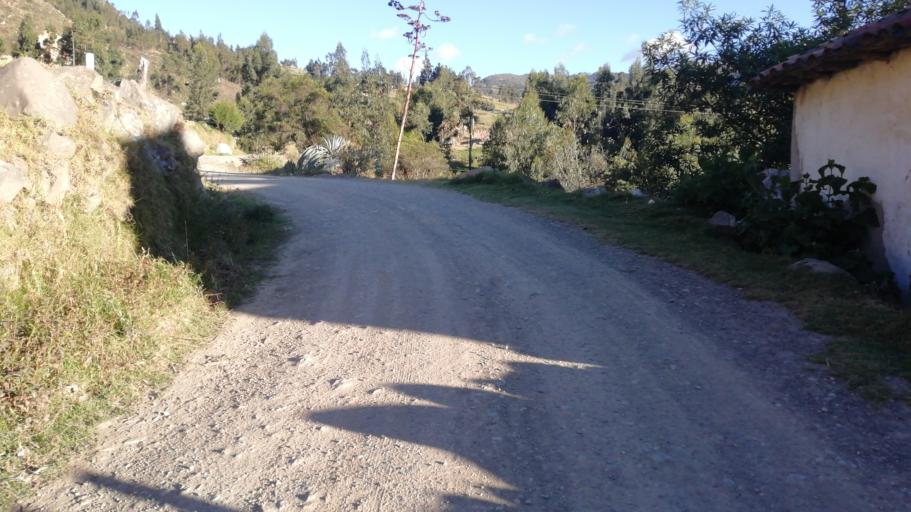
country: CO
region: Boyaca
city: Gameza
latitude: 5.7855
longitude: -72.8007
